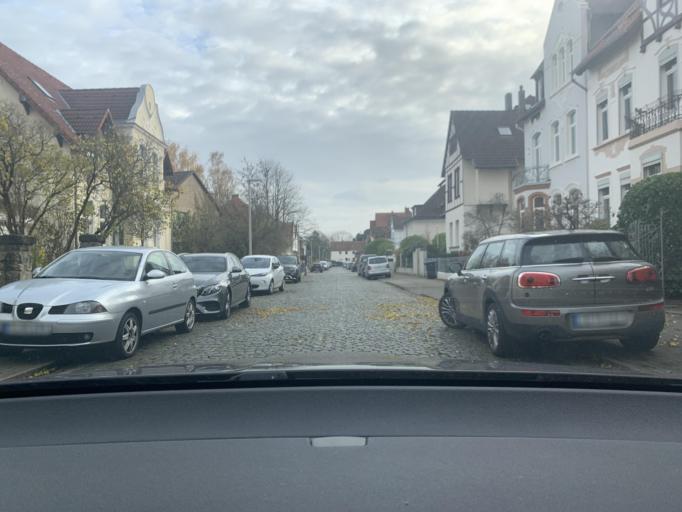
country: DE
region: Lower Saxony
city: Laatzen
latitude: 52.3496
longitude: 9.7765
